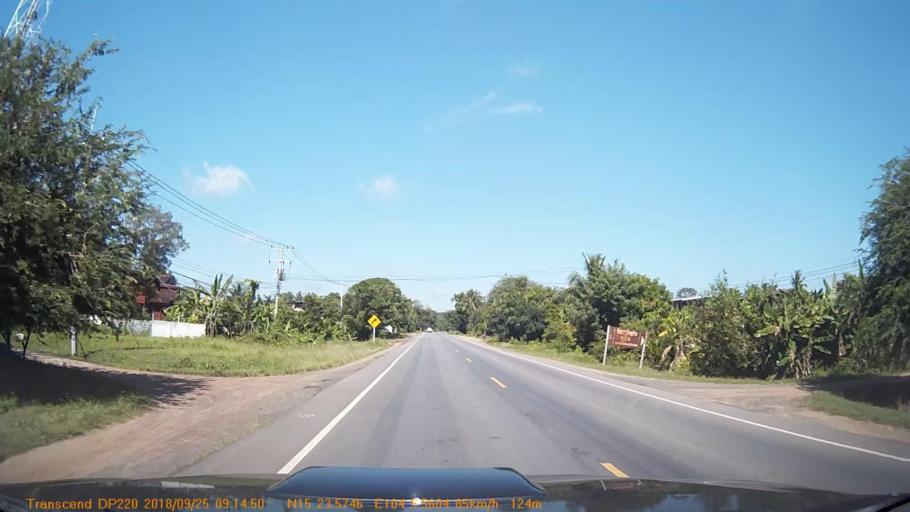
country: TH
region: Sisaket
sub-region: Amphoe Bueng Bun
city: Bueng Bun
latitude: 15.3930
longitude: 104.0925
